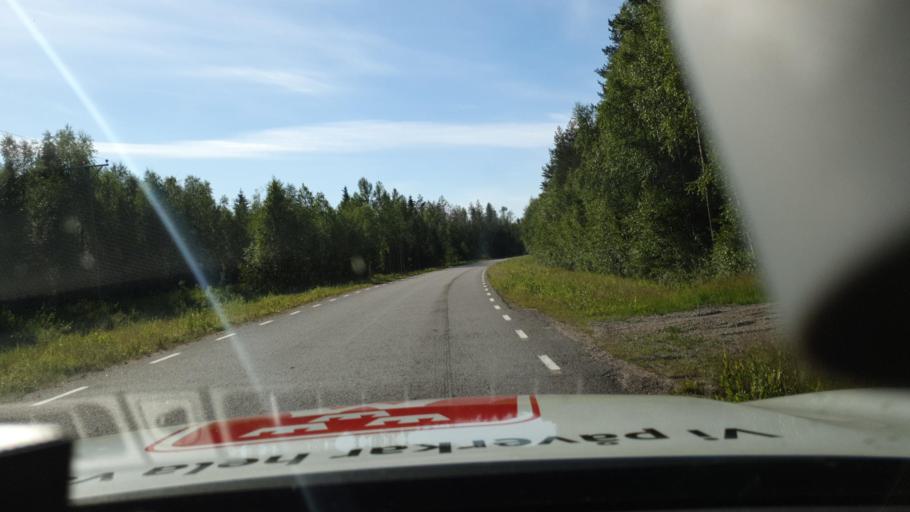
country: SE
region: Norrbotten
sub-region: Kalix Kommun
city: Toere
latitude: 65.8966
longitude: 22.6257
